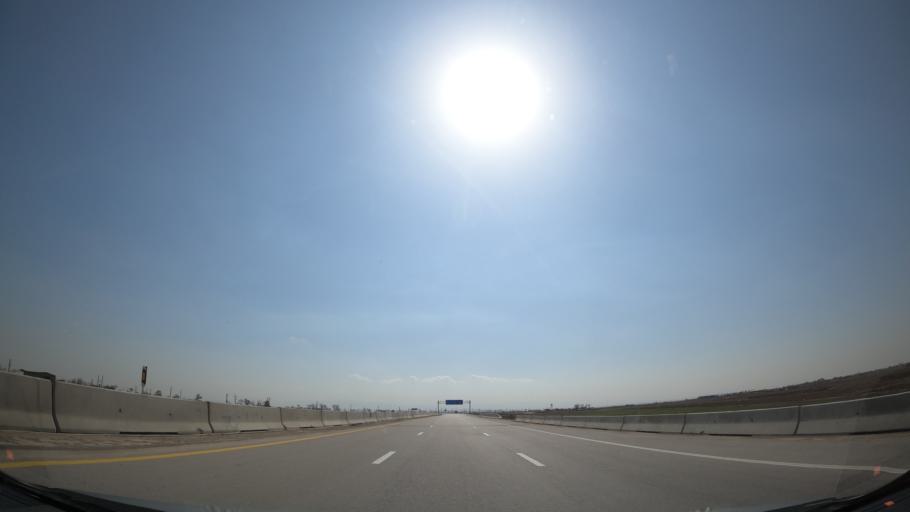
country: IR
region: Qazvin
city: Abyek
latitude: 35.9737
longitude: 50.4614
